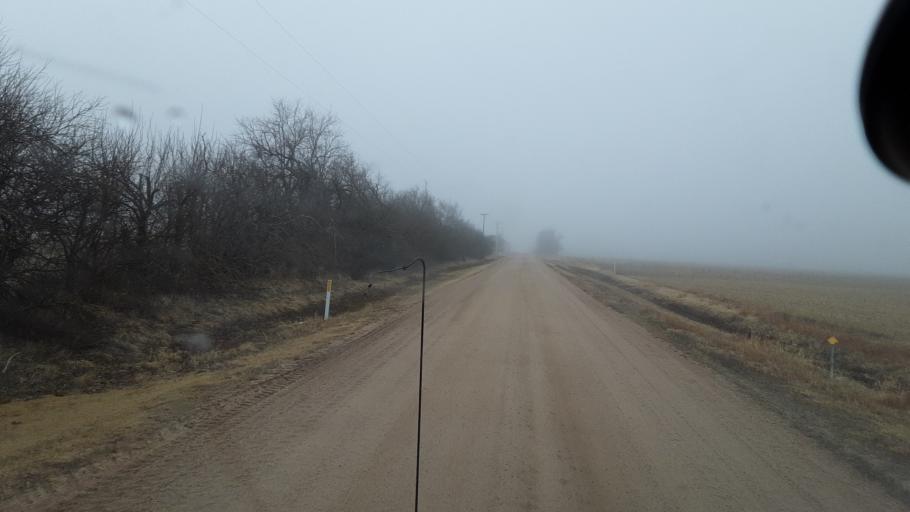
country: US
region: Kansas
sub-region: Reno County
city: South Hutchinson
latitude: 38.0015
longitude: -97.9955
